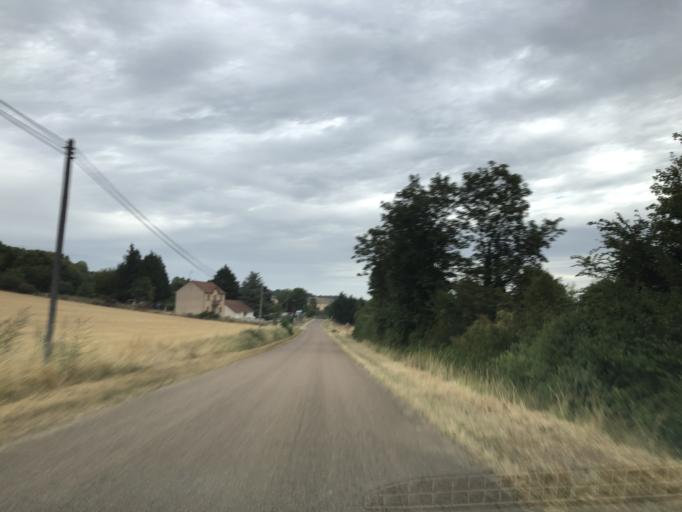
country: FR
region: Bourgogne
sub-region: Departement de l'Yonne
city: Aillant-sur-Tholon
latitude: 47.9129
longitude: 3.3228
